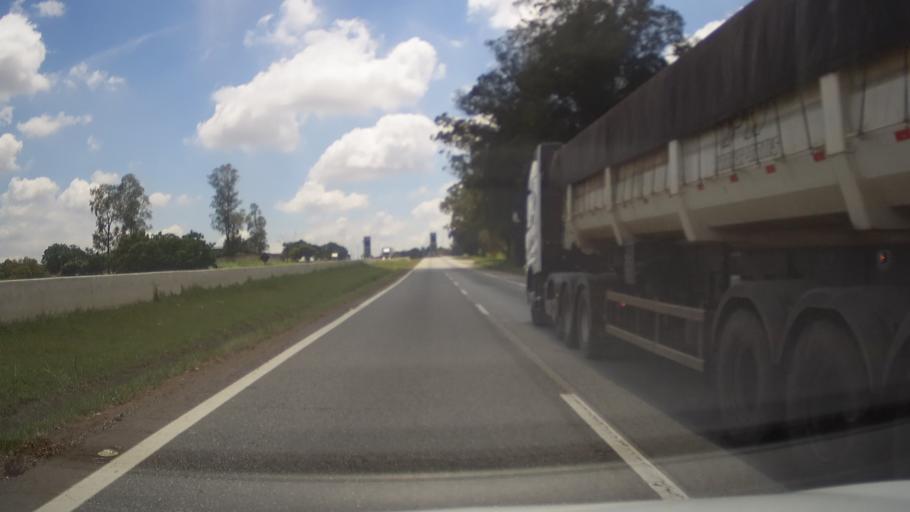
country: BR
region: Minas Gerais
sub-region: Sao Goncalo Do Sapucai
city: Sao Goncalo do Sapucai
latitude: -21.9487
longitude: -45.6228
